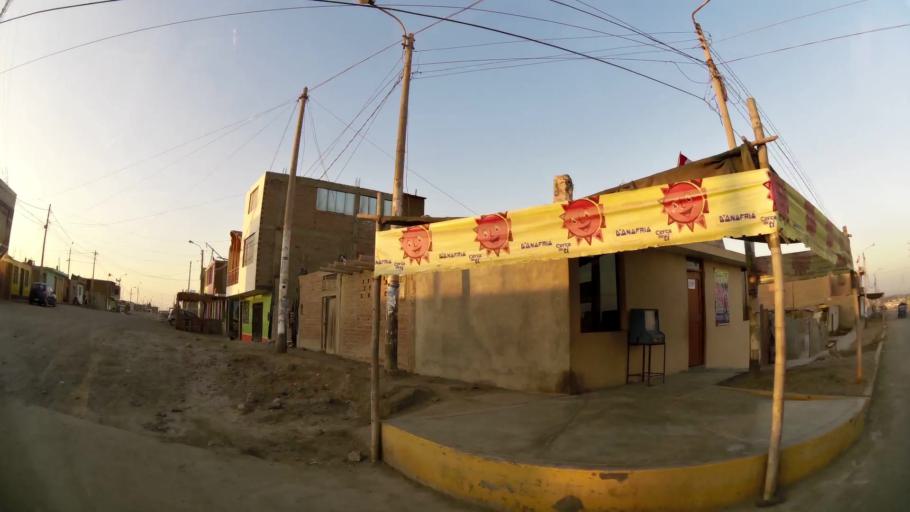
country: PE
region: Ica
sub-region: Provincia de Pisco
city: San Clemente
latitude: -13.6780
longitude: -76.1546
